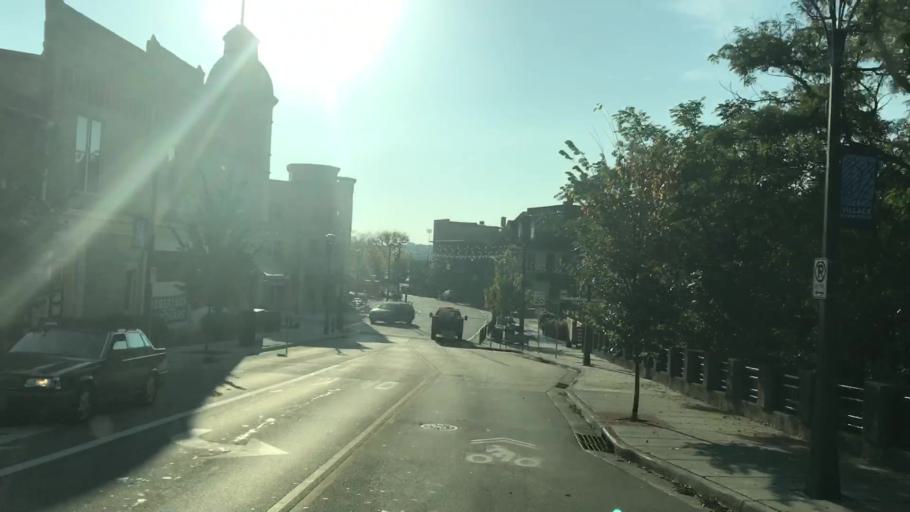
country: US
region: Wisconsin
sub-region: Milwaukee County
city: Wauwatosa
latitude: 43.0500
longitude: -88.0091
